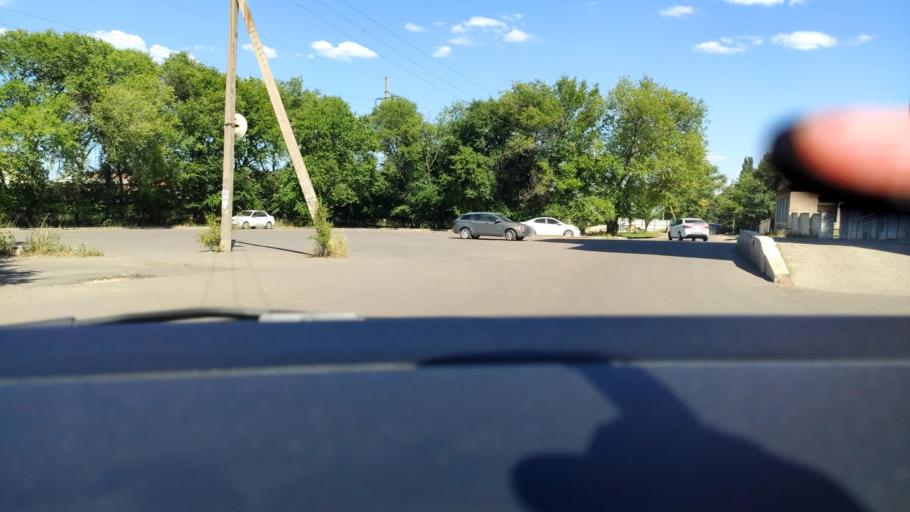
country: RU
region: Voronezj
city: Semiluki
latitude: 51.7023
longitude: 39.0237
